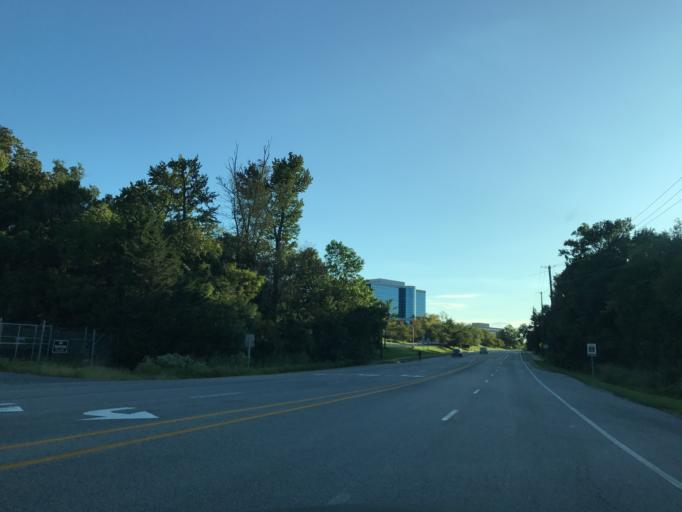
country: US
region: Maryland
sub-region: Prince George's County
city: Greenbelt
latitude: 39.0117
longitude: -76.8926
